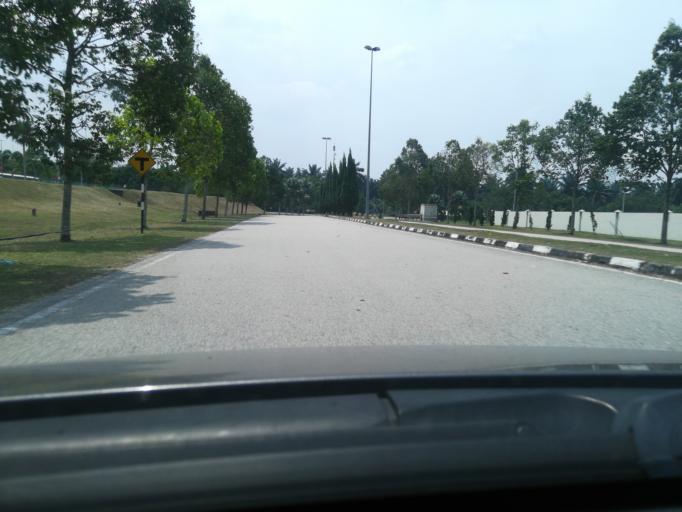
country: MY
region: Kedah
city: Kulim
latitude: 5.4300
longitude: 100.5776
